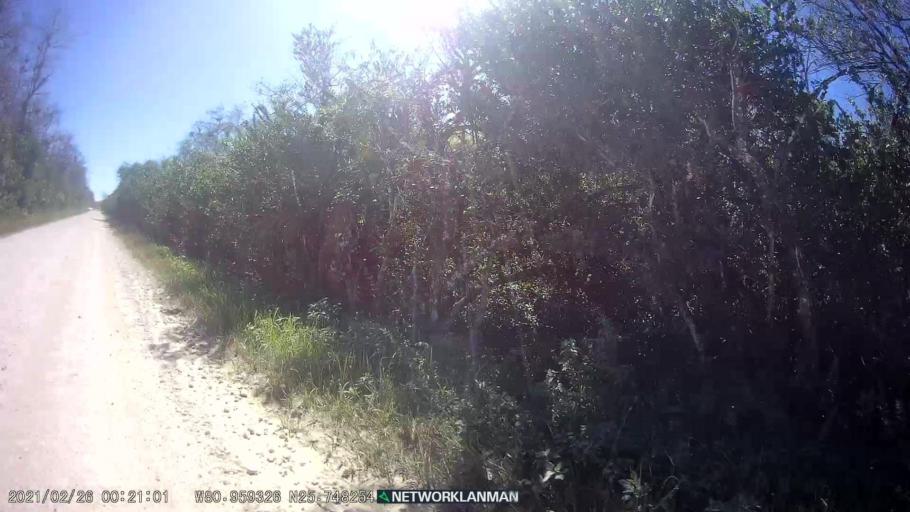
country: US
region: Florida
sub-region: Miami-Dade County
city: The Hammocks
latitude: 25.7482
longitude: -80.9592
